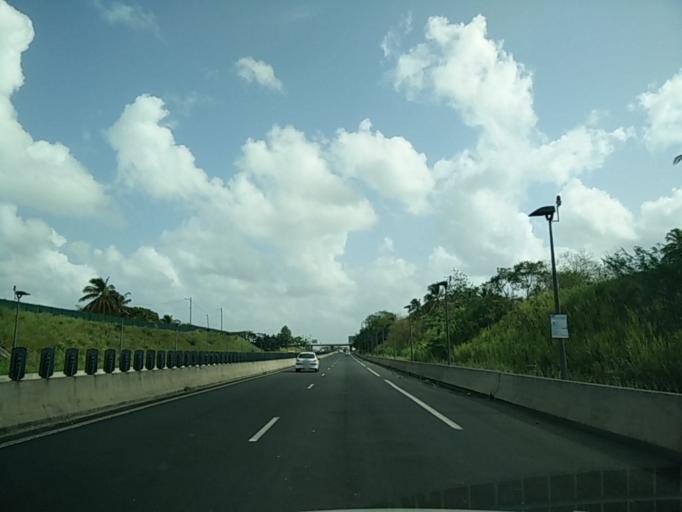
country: GP
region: Guadeloupe
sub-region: Guadeloupe
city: Les Abymes
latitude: 16.2608
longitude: -61.5109
